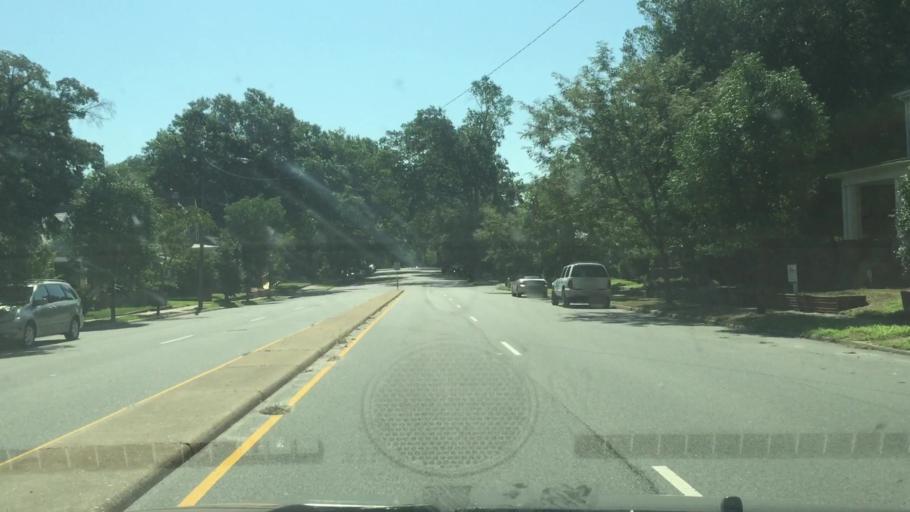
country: US
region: Virginia
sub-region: Henrico County
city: Dumbarton
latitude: 37.5692
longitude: -77.4957
